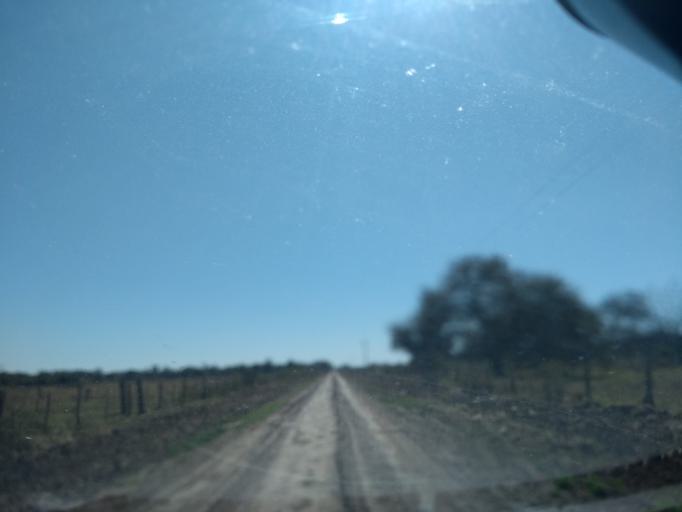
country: AR
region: Chaco
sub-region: Departamento de Quitilipi
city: Quitilipi
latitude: -26.7440
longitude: -60.2375
